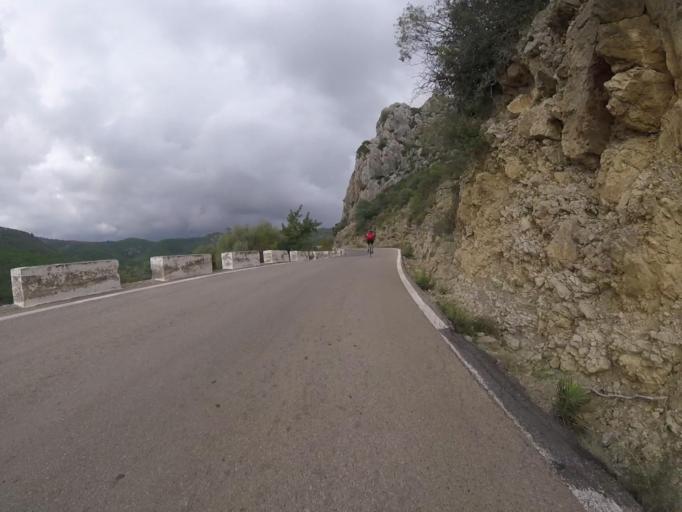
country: ES
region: Valencia
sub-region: Provincia de Castello
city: Cabanes
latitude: 40.1427
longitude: 0.0953
